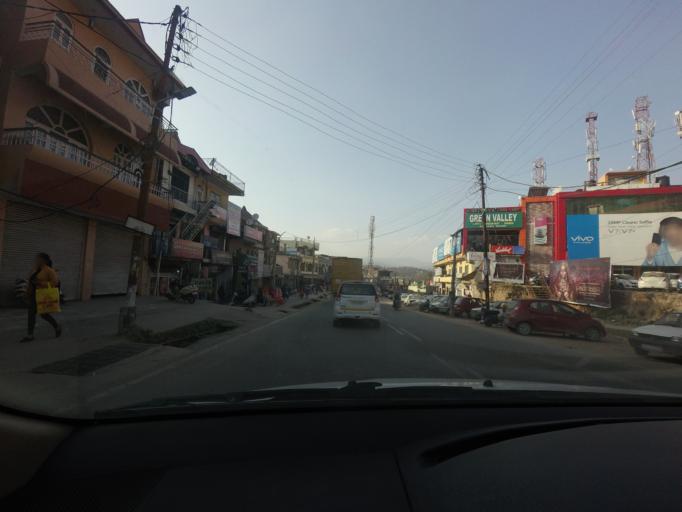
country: IN
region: Himachal Pradesh
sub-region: Mandi
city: Sundarnagar
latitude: 31.5302
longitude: 76.8886
